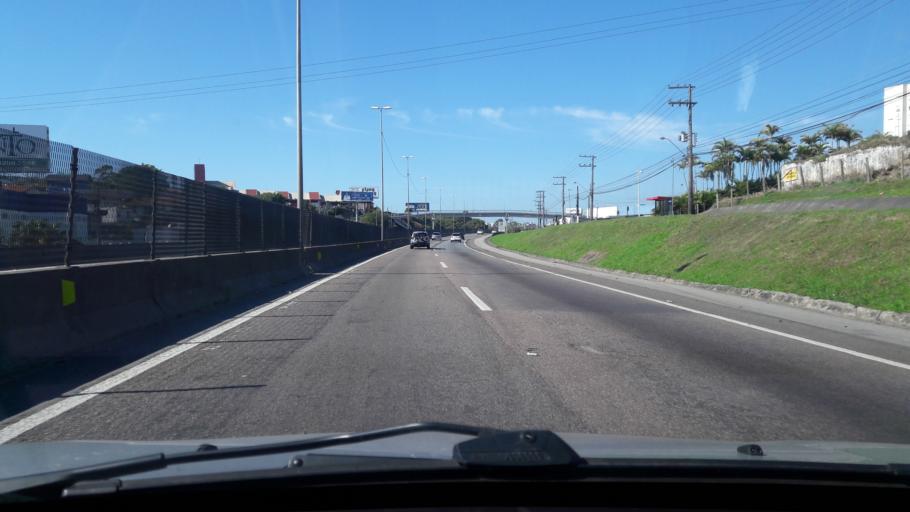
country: BR
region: Santa Catarina
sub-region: Sao Jose
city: Campinas
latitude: -27.5435
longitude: -48.6207
